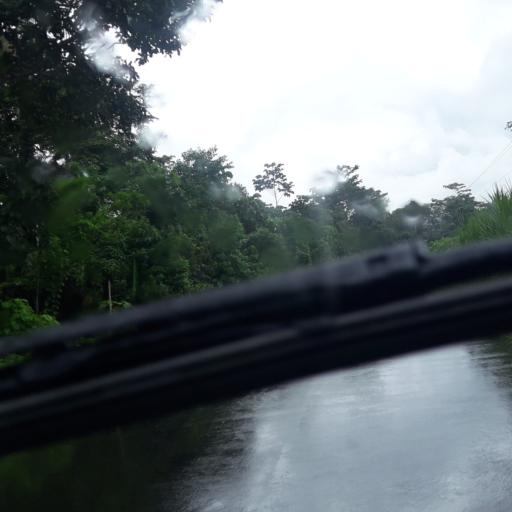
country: EC
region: Napo
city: Tena
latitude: -1.0403
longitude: -77.6639
